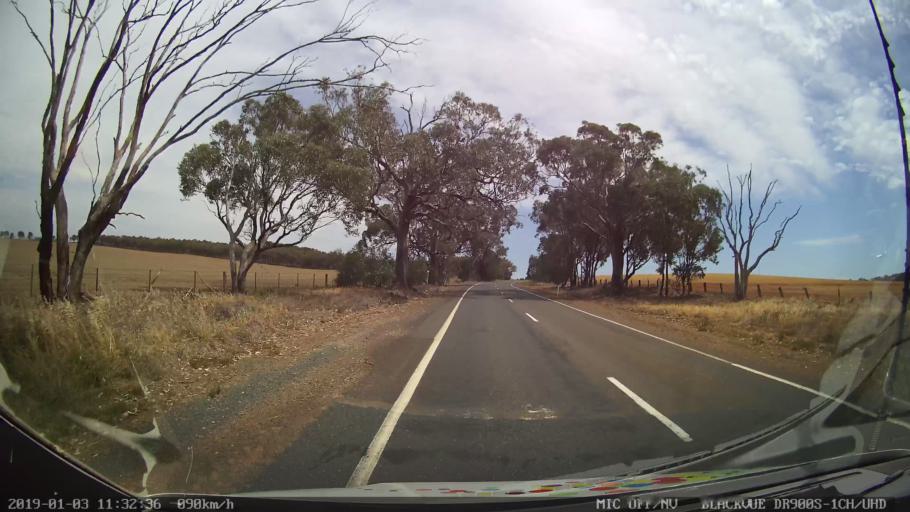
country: AU
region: New South Wales
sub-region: Weddin
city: Grenfell
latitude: -33.9562
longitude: 148.1775
